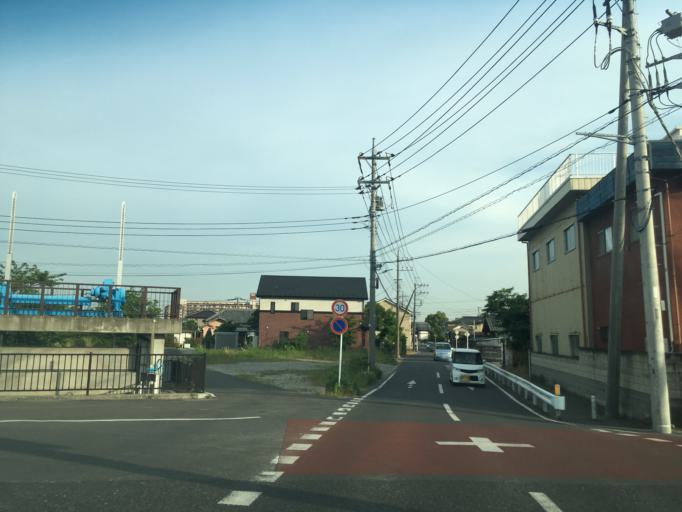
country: JP
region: Saitama
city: Yoshikawa
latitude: 35.8692
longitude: 139.8181
